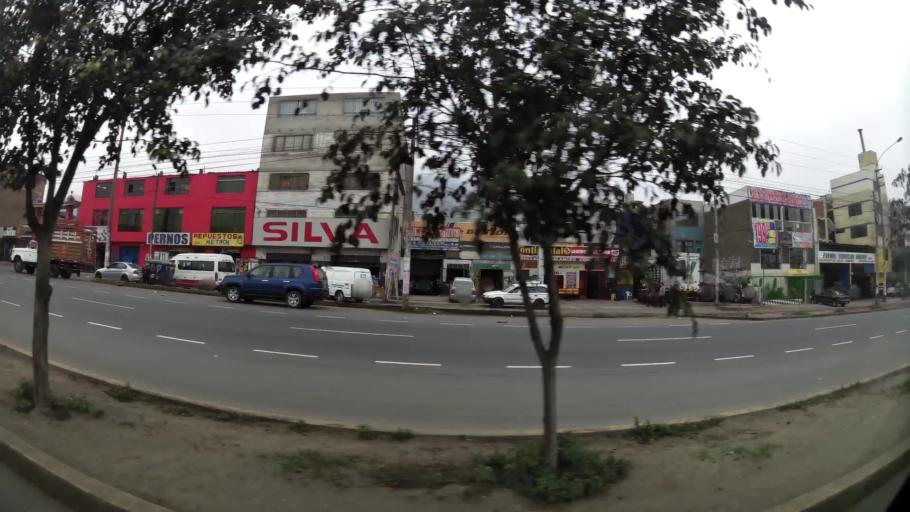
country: PE
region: Lima
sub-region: Lima
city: Urb. Santo Domingo
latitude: -11.9292
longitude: -77.0436
